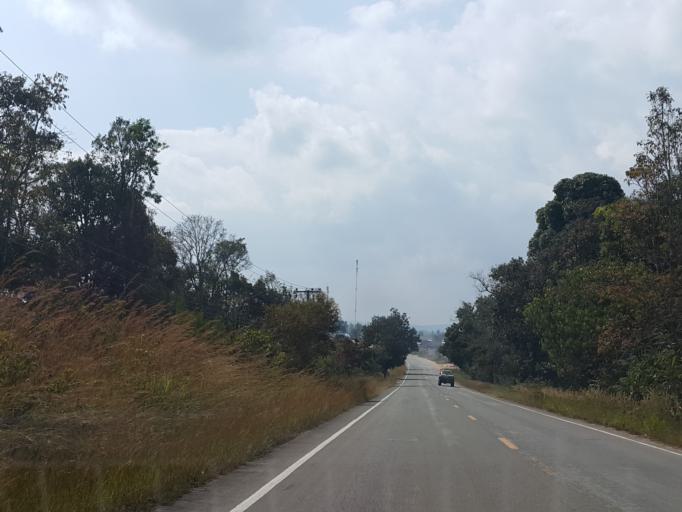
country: TH
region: Chiang Mai
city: Hot
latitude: 18.0960
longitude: 98.3678
